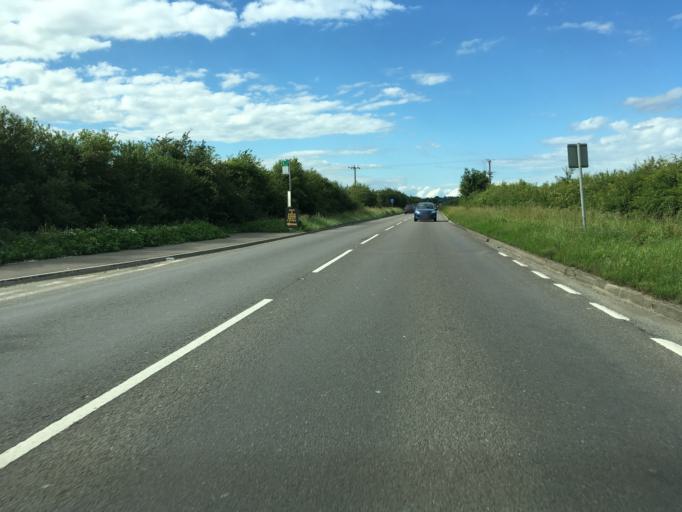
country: GB
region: England
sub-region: Buckinghamshire
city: Aylesbury
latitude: 51.8438
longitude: -0.7737
